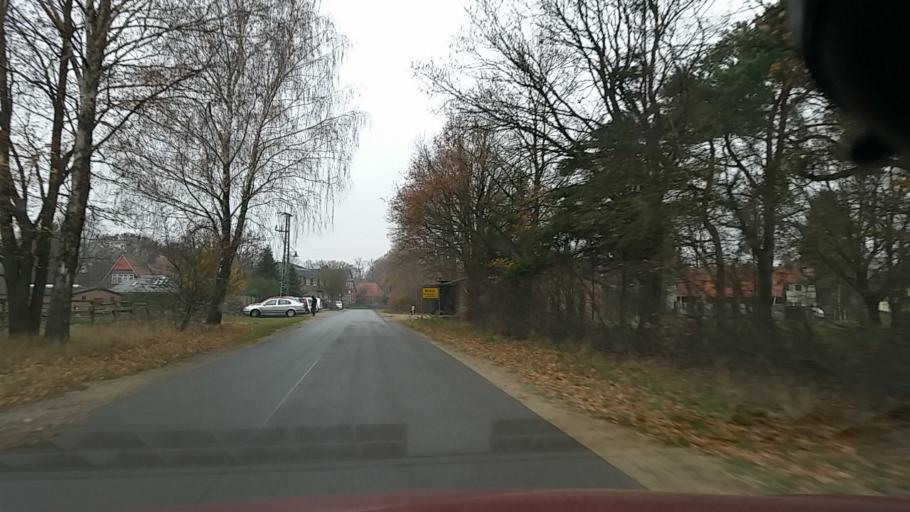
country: DE
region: Lower Saxony
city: Obernholz
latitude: 52.8057
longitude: 10.5496
